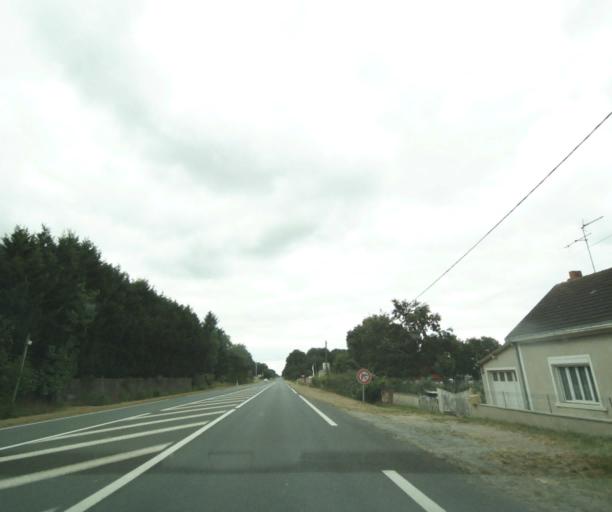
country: FR
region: Pays de la Loire
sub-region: Departement de Maine-et-Loire
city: Pellouailles-les-Vignes
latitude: 47.5132
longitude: -0.4626
